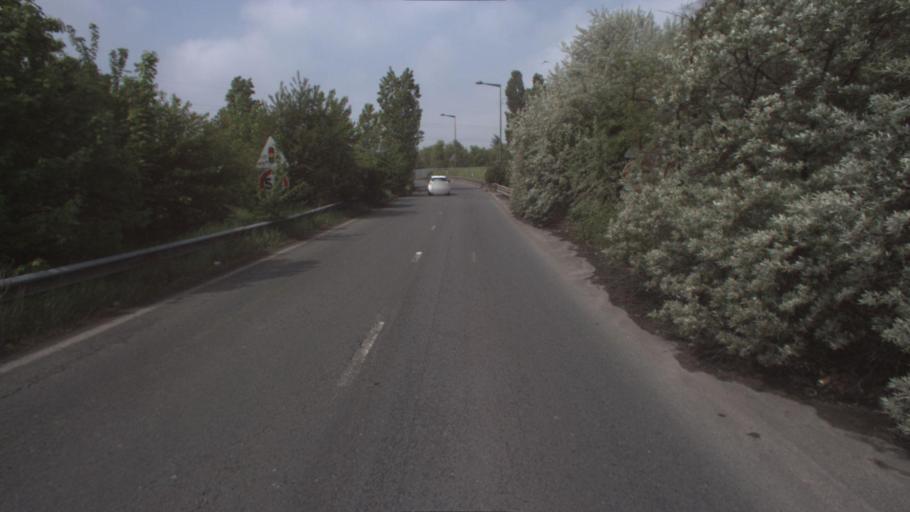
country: FR
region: Ile-de-France
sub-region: Departement de Seine-Saint-Denis
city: Sevran
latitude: 48.9552
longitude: 2.5121
